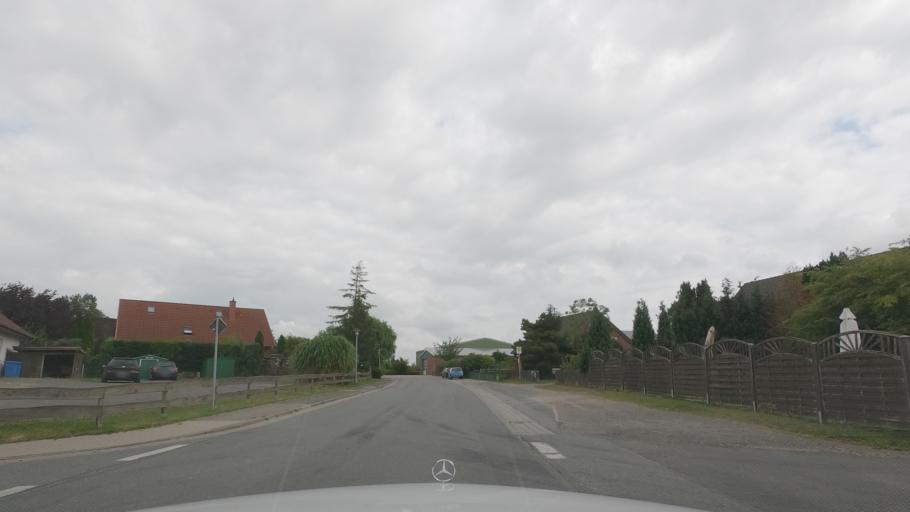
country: DE
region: Lower Saxony
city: Uthlede
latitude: 53.2956
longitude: 8.5299
